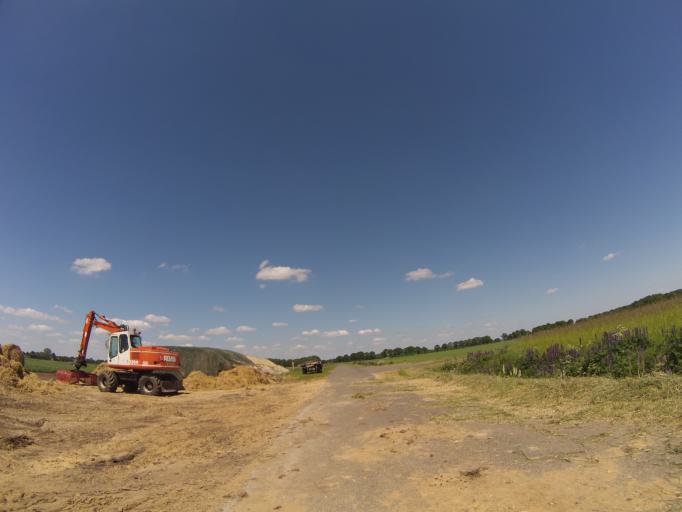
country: NL
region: Drenthe
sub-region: Gemeente Hoogeveen
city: Hoogeveen
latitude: 52.7937
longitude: 6.6147
